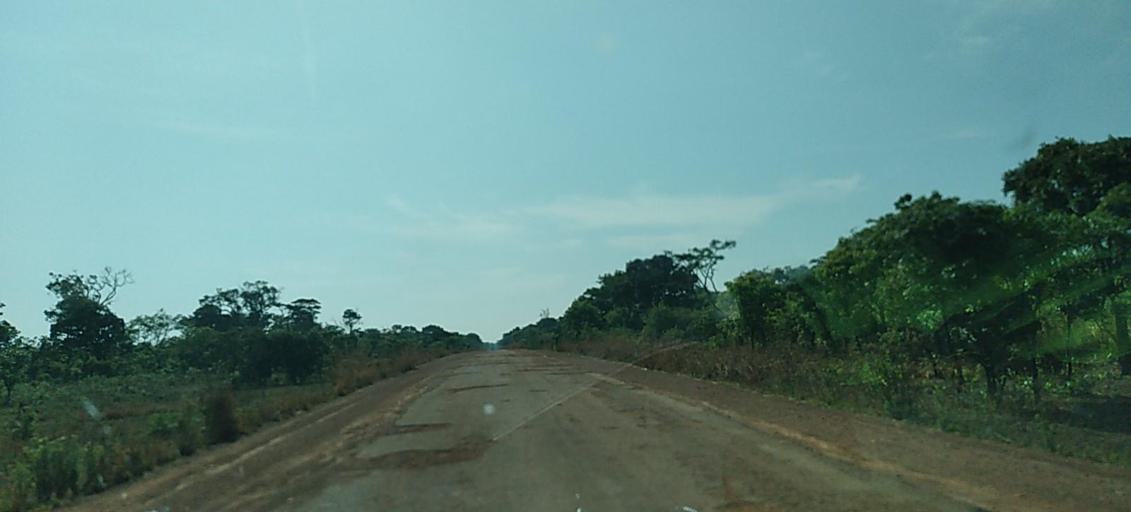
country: ZM
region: North-Western
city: Mwinilunga
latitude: -11.7885
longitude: 25.0561
